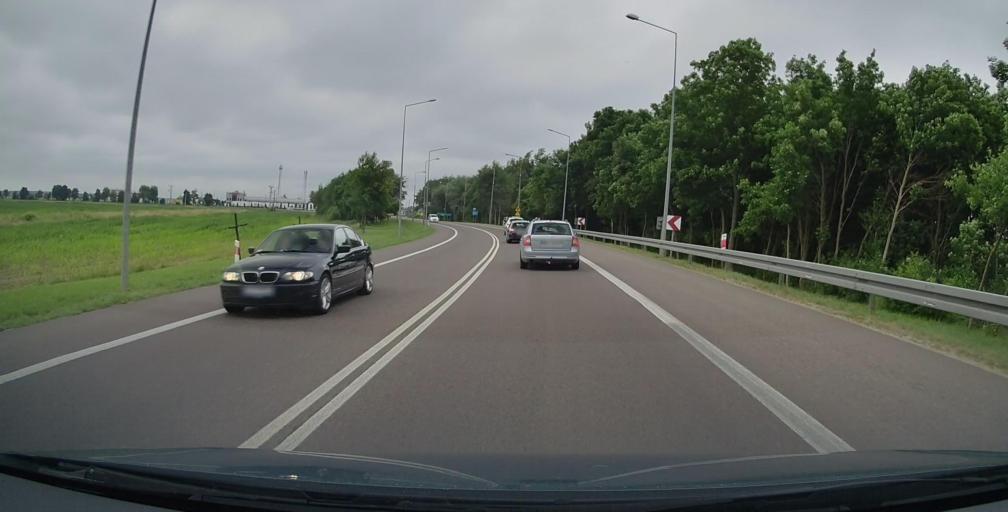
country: PL
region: Lublin Voivodeship
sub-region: Powiat bialski
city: Miedzyrzec Podlaski
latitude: 52.0007
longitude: 22.7585
